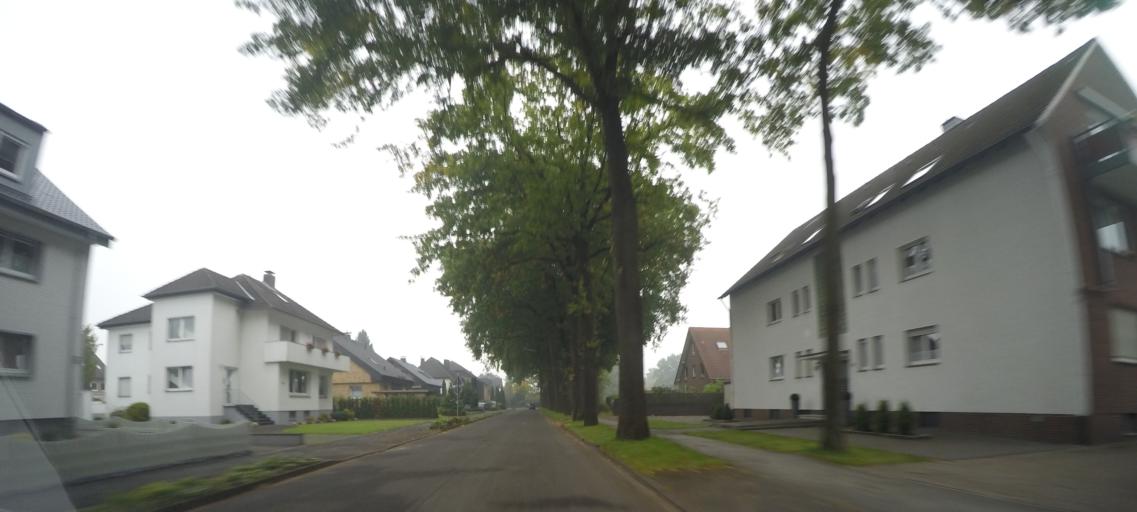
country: DE
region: North Rhine-Westphalia
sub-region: Regierungsbezirk Arnsberg
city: Lippstadt
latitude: 51.6850
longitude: 8.3059
